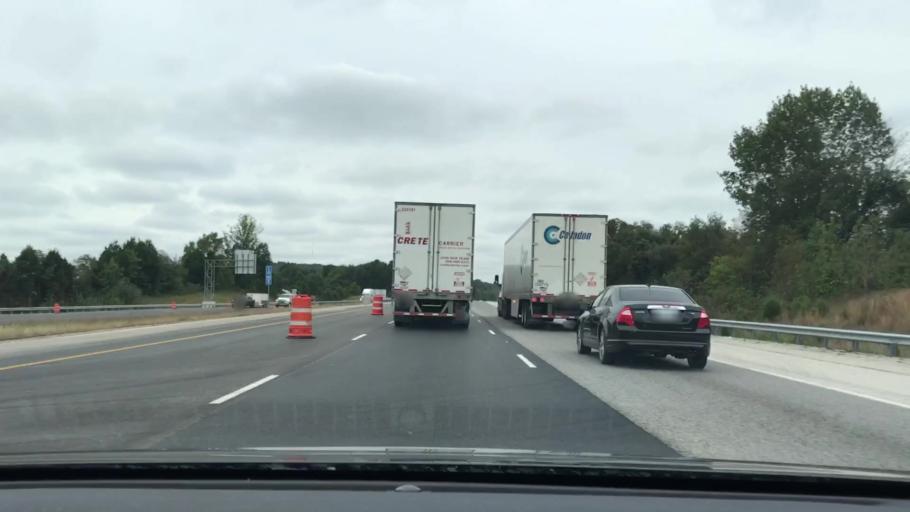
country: US
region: Kentucky
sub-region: Edmonson County
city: Brownsville
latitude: 37.0488
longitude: -86.1505
